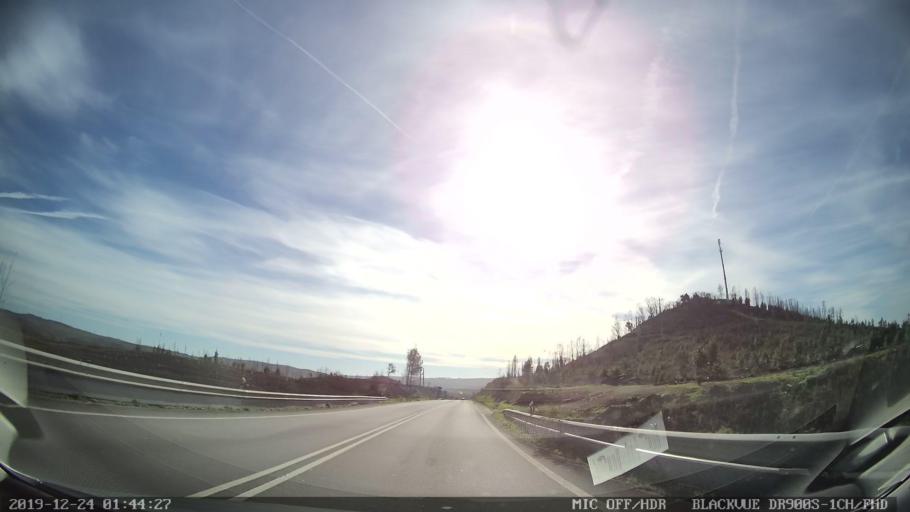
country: PT
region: Portalegre
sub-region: Nisa
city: Nisa
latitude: 39.5548
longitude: -7.7939
